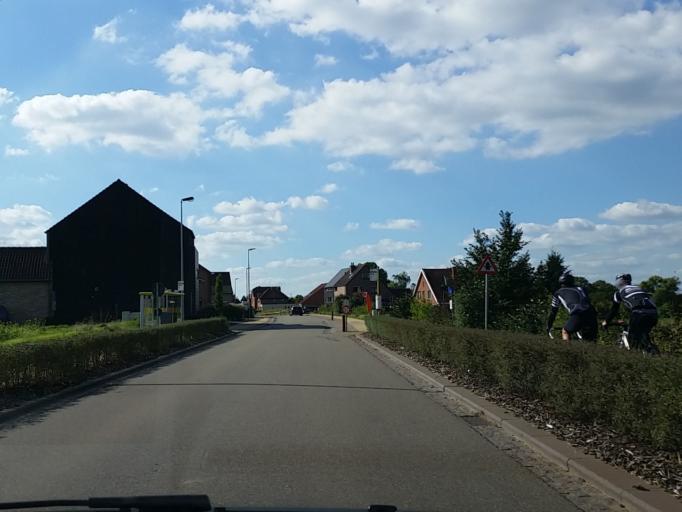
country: BE
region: Flanders
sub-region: Provincie Vlaams-Brabant
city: Holsbeek
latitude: 50.9208
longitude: 4.7734
